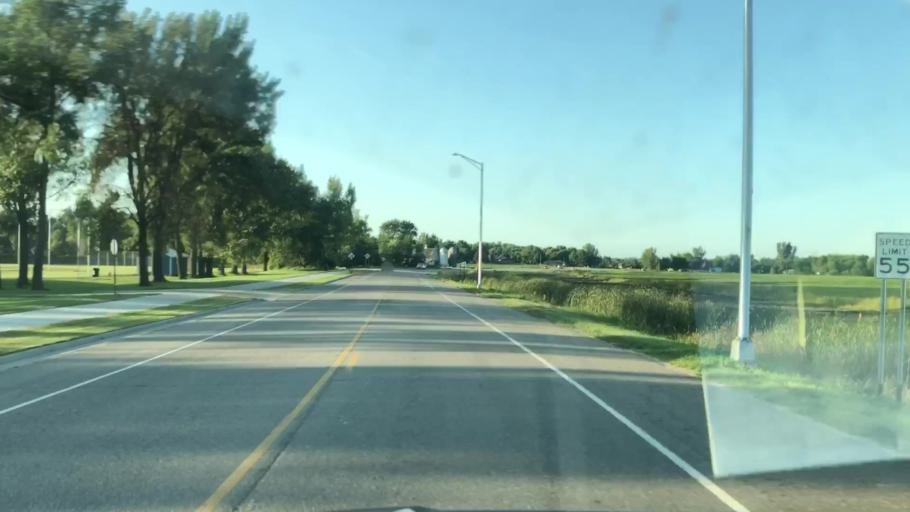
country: US
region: Minnesota
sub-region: Nobles County
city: Worthington
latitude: 43.6224
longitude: -95.6336
